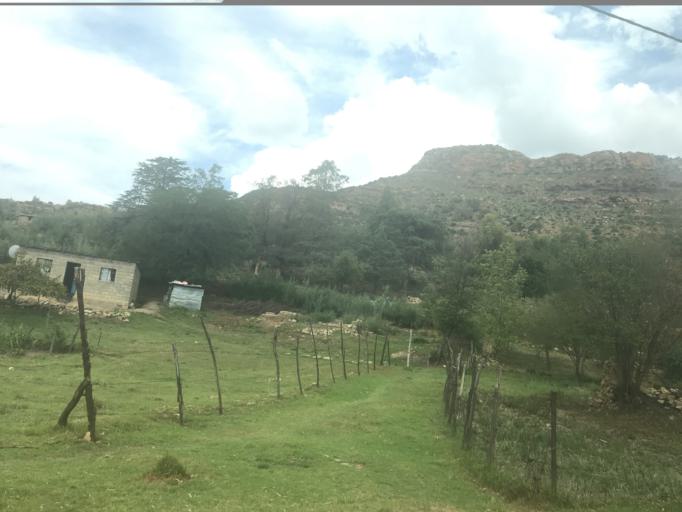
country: LS
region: Maseru
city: Nako
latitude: -29.6302
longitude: 27.5136
